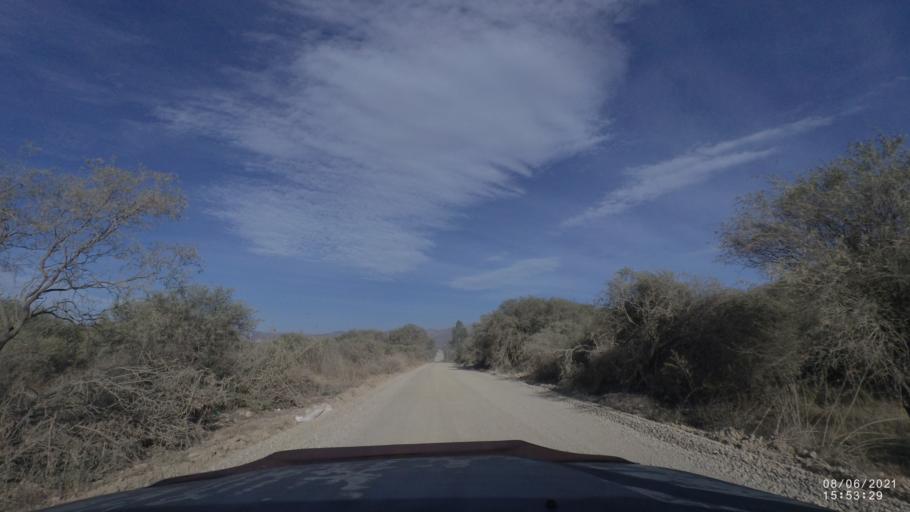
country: BO
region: Cochabamba
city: Capinota
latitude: -17.5530
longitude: -66.2573
